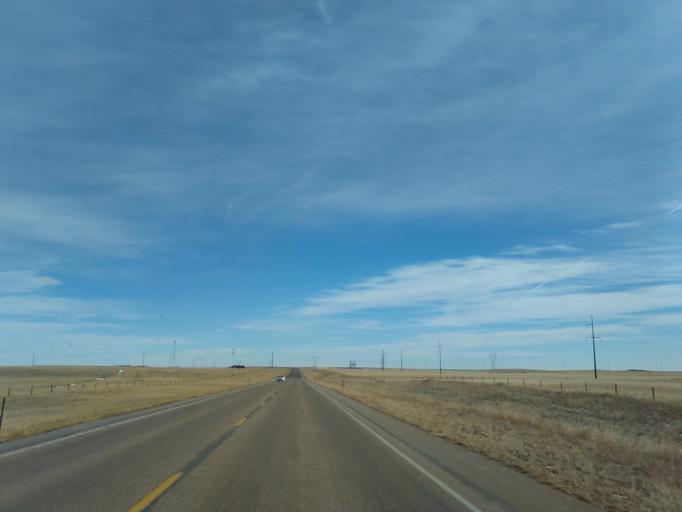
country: US
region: Wyoming
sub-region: Laramie County
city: Pine Bluffs
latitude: 41.4349
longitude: -104.3617
